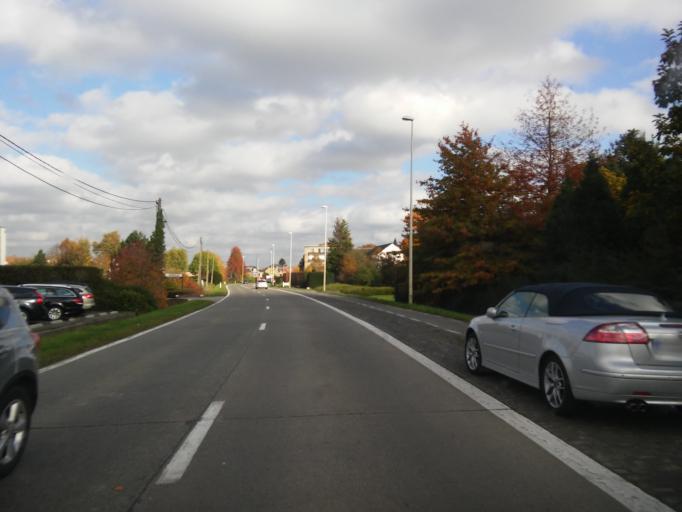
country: BE
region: Flanders
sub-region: Provincie Antwerpen
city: Lier
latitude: 51.1219
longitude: 4.5453
